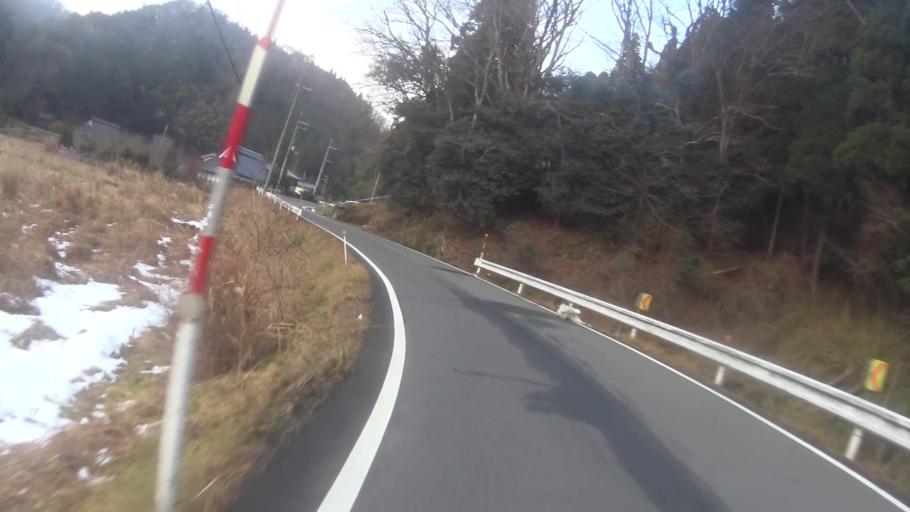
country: JP
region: Kyoto
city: Maizuru
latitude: 35.4124
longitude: 135.4616
